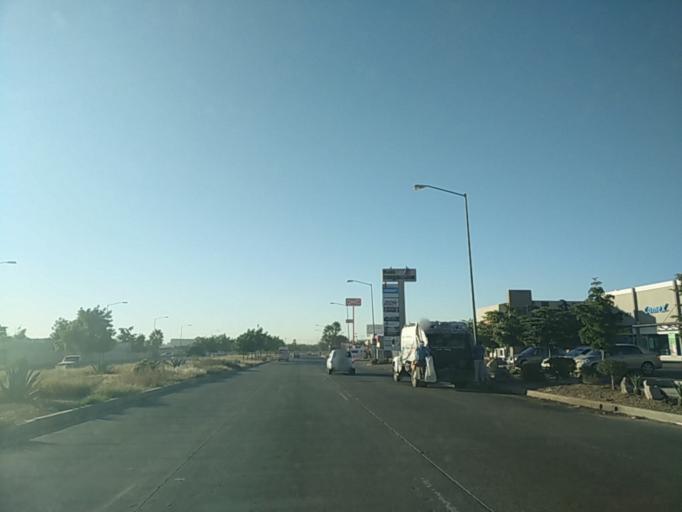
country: MX
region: Sonora
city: Hermosillo
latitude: 29.0913
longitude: -111.0223
